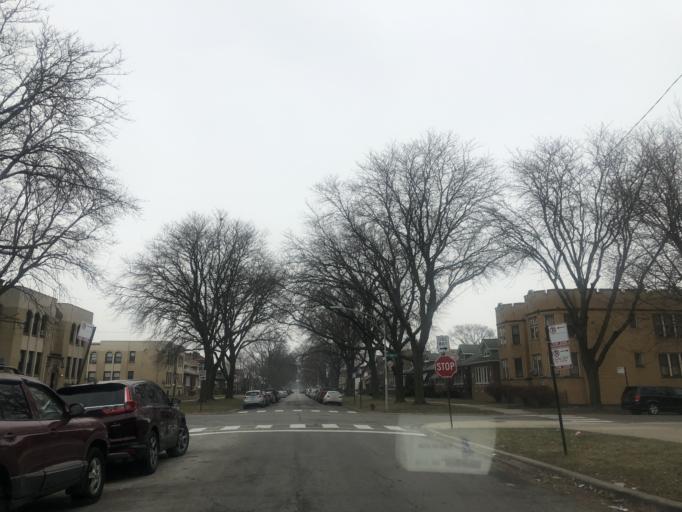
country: US
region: Illinois
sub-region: Cook County
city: Evergreen Park
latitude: 41.7526
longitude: -87.6182
